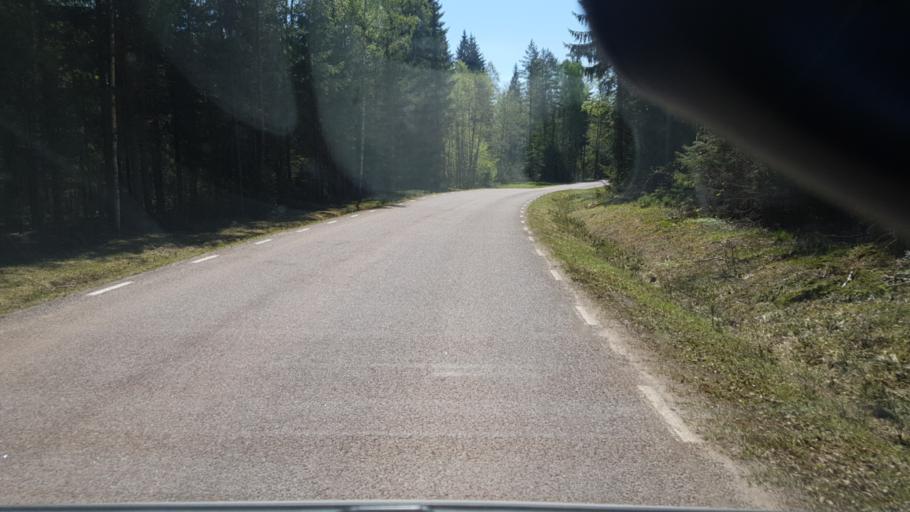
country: SE
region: Vaermland
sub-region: Arvika Kommun
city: Arvika
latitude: 59.7901
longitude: 12.8389
